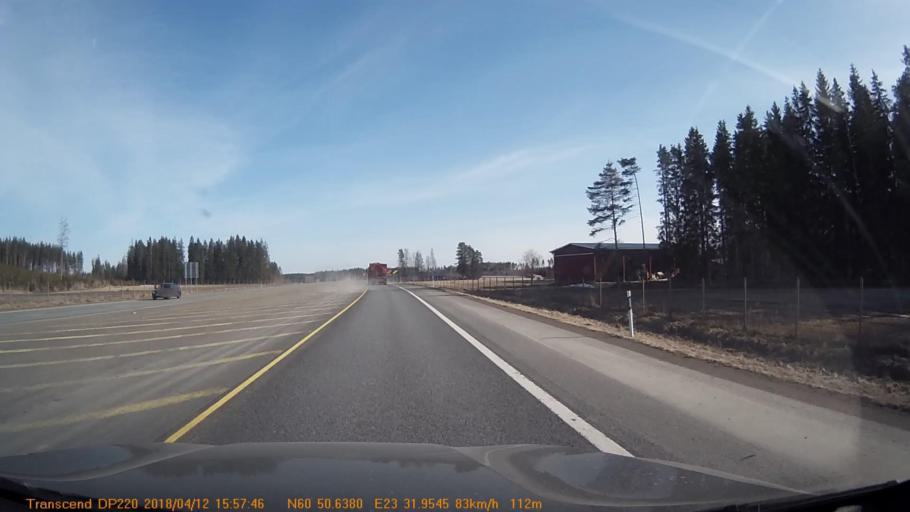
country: FI
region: Haeme
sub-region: Forssa
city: Jokioinen
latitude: 60.8437
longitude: 23.5330
